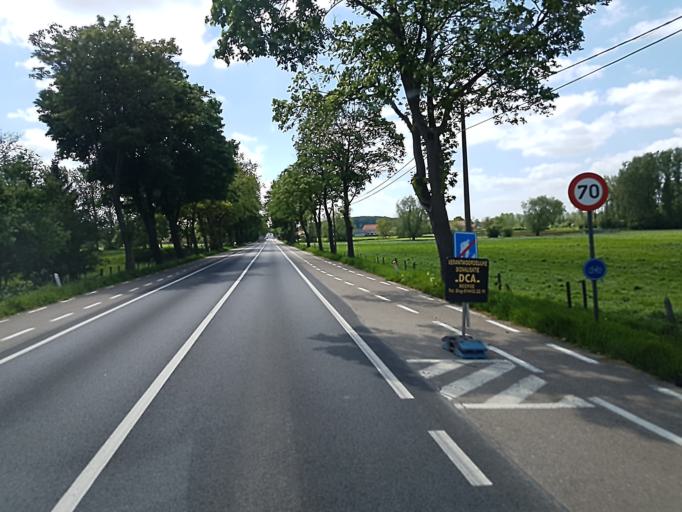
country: BE
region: Flanders
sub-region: Provincie Vlaams-Brabant
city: Glabbeek-Zuurbemde
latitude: 50.8595
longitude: 4.9545
